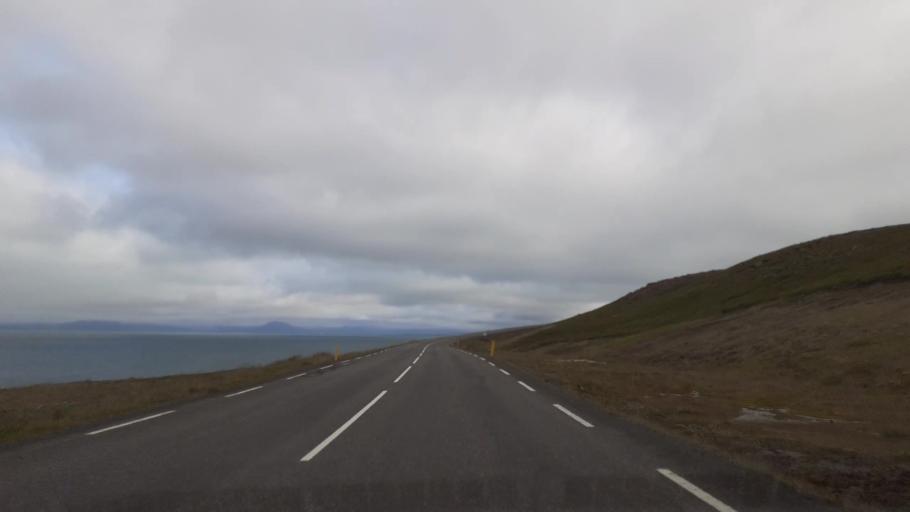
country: IS
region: Northeast
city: Husavik
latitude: 66.1888
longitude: -16.9973
